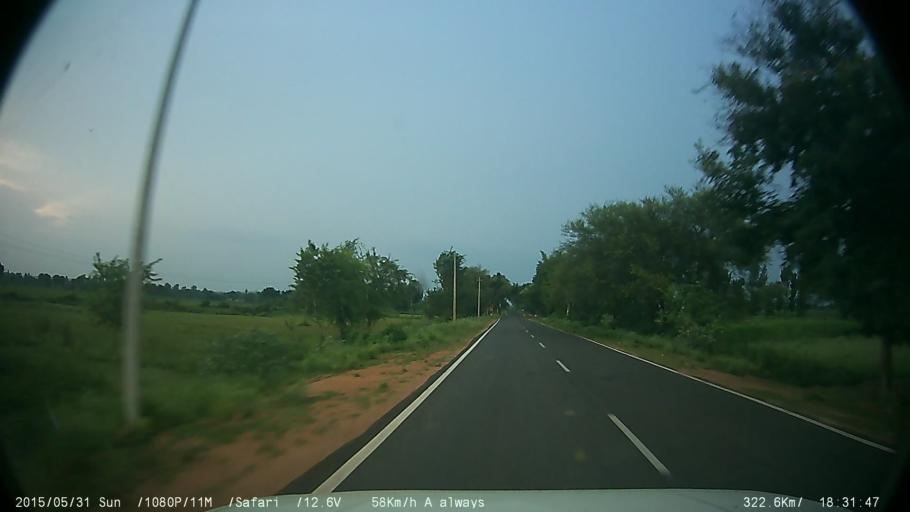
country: IN
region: Karnataka
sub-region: Mysore
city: Nanjangud
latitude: 12.1287
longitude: 76.7464
